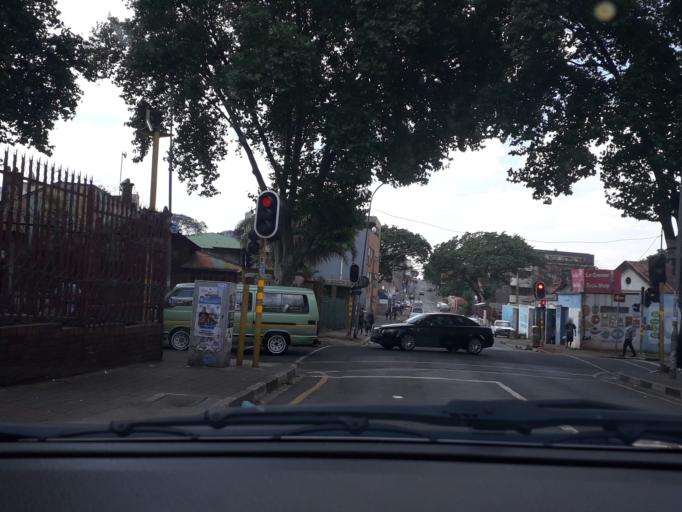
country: ZA
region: Gauteng
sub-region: City of Johannesburg Metropolitan Municipality
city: Johannesburg
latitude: -26.1808
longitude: 28.0687
